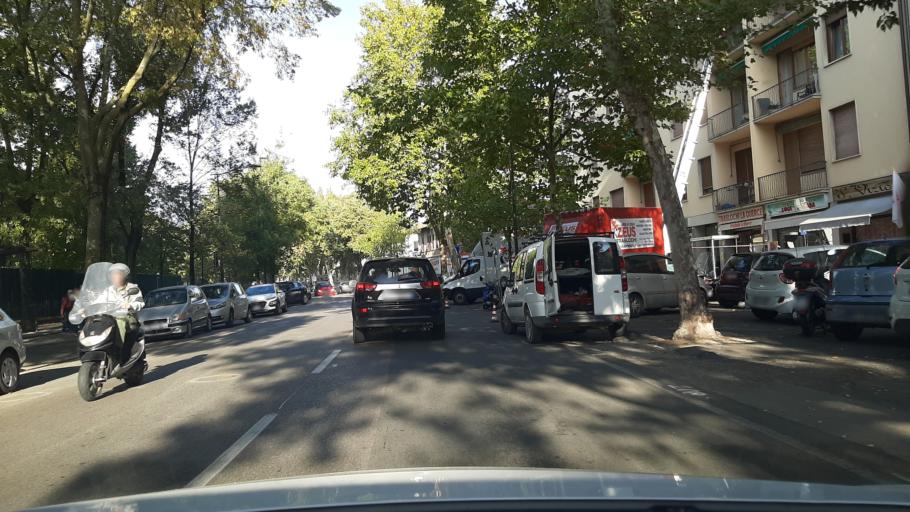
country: IT
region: Tuscany
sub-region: Province of Florence
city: Fiesole
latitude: 43.7814
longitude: 11.2871
